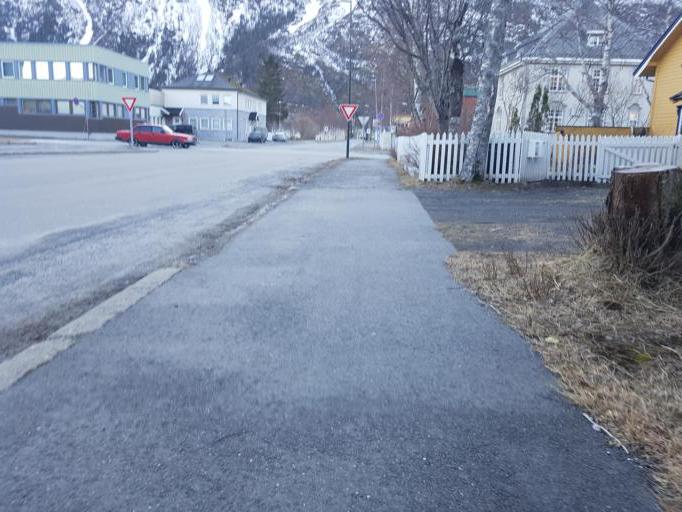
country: NO
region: Nordland
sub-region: Vefsn
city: Mosjoen
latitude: 65.8380
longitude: 13.1970
